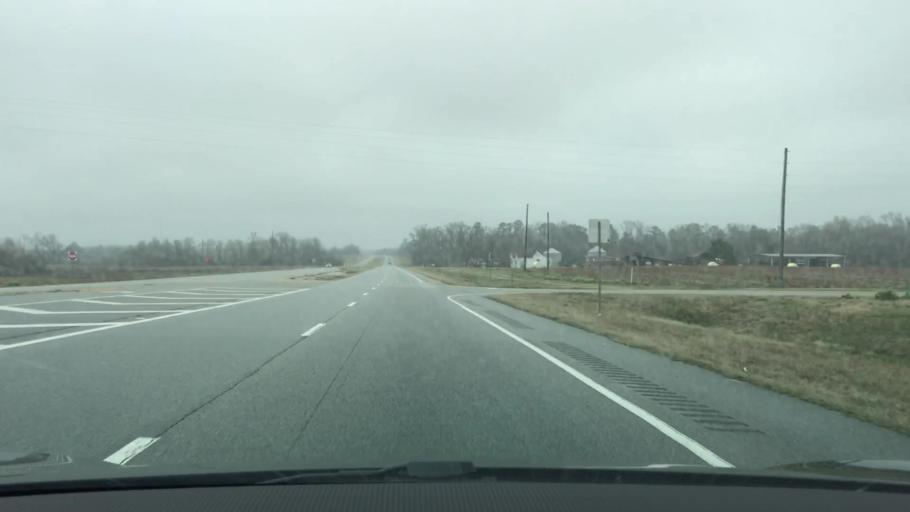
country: US
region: Georgia
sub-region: Jefferson County
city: Wadley
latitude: 32.8301
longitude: -82.4018
